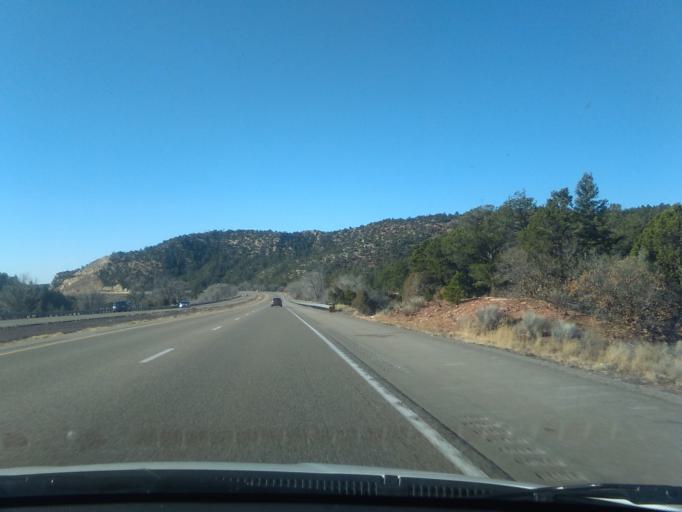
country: US
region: New Mexico
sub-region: Santa Fe County
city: Eldorado at Santa Fe
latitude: 35.5602
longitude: -105.8115
